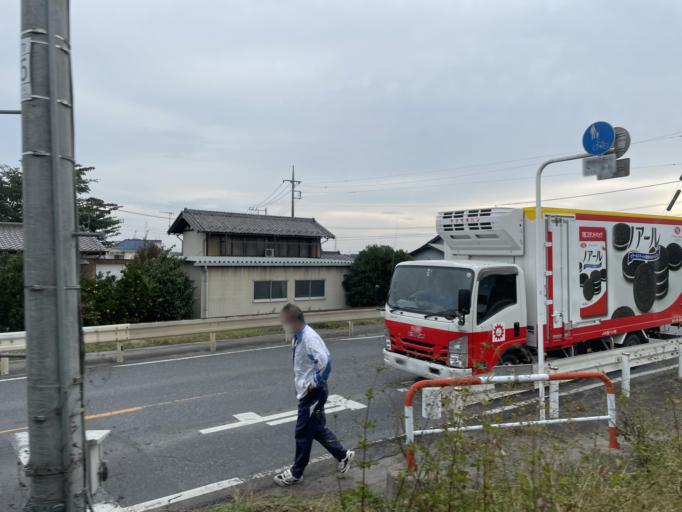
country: JP
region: Saitama
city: Yorii
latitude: 36.1498
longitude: 139.2033
